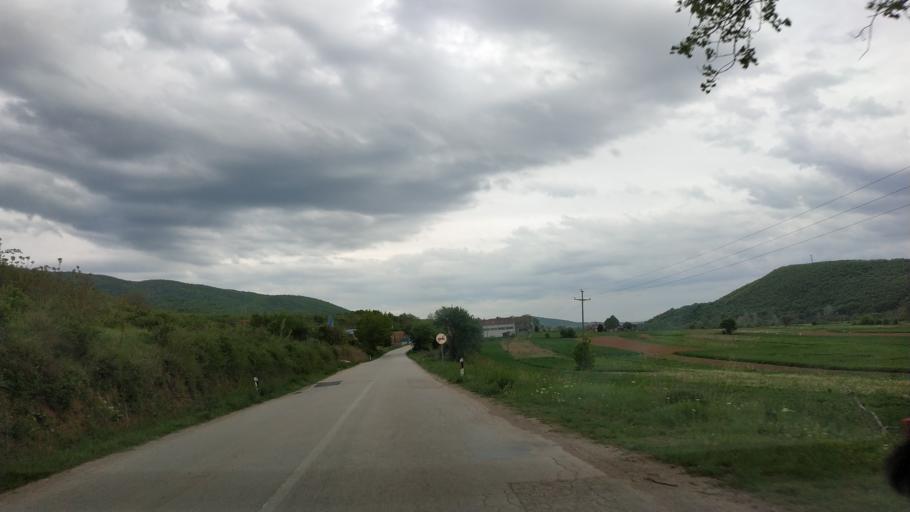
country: RS
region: Central Serbia
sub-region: Nisavski Okrug
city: Aleksinac
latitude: 43.5987
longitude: 21.6878
